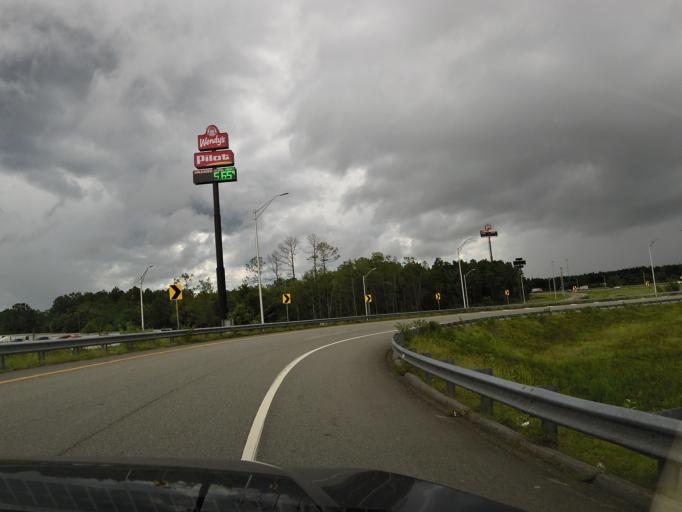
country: US
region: Georgia
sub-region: Camden County
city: Kingsland
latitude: 30.7597
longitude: -81.6541
